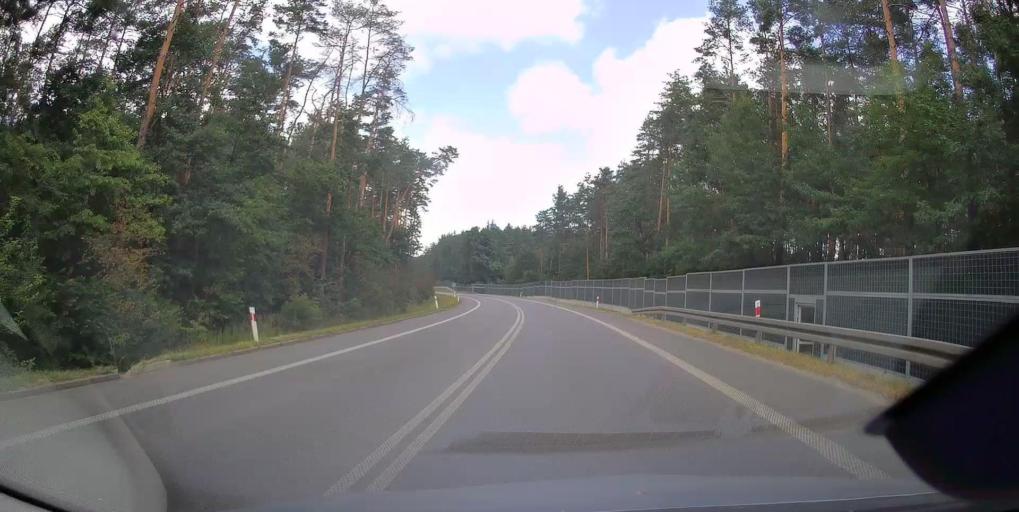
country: PL
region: Subcarpathian Voivodeship
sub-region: Powiat mielecki
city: Mielec
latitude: 50.2824
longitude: 21.4989
